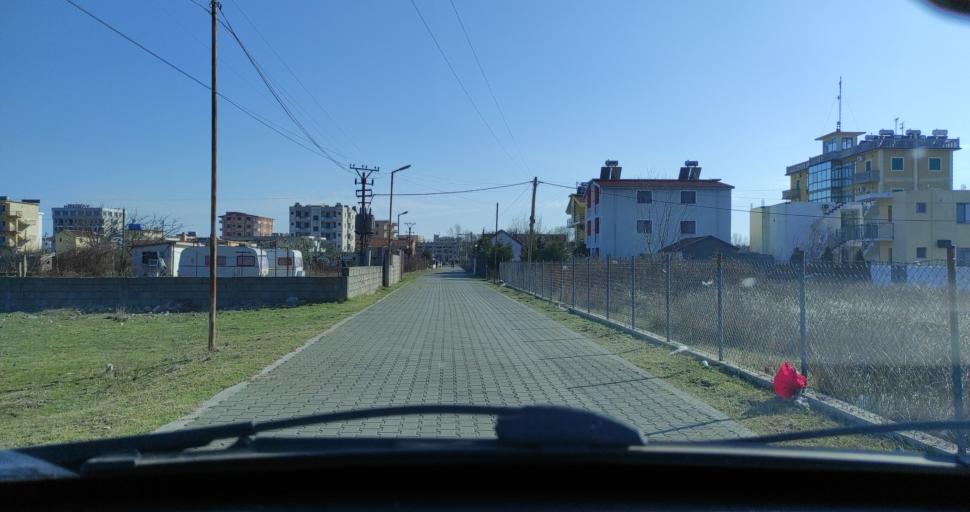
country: AL
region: Shkoder
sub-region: Rrethi i Shkodres
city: Velipoje
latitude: 41.8689
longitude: 19.4212
